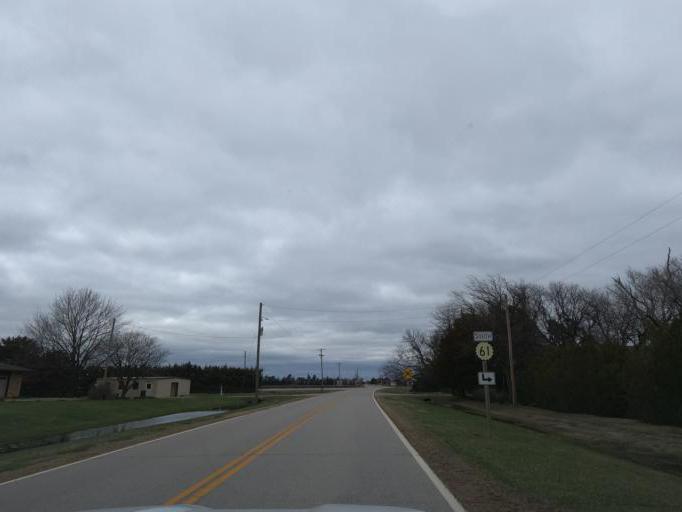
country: US
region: Kansas
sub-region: Reno County
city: South Hutchinson
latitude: 37.9861
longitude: -98.0502
